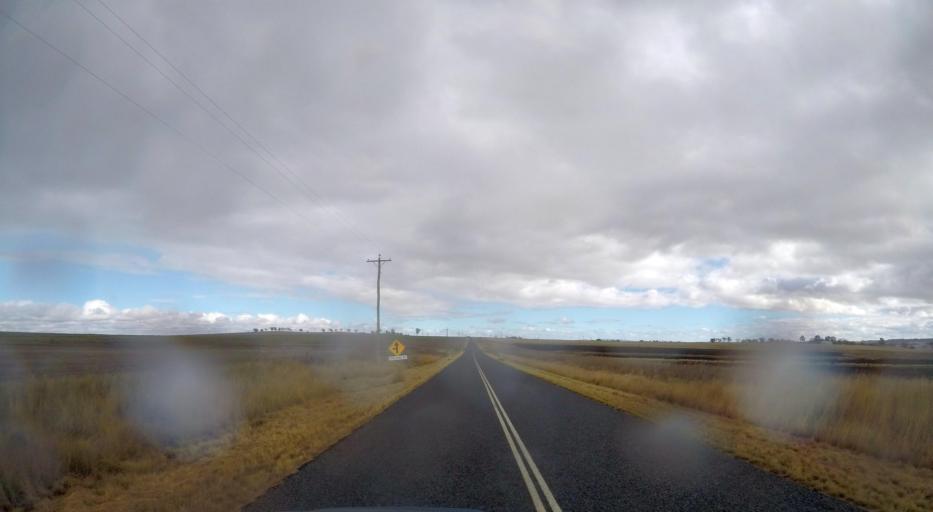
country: AU
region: Queensland
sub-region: Southern Downs
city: Warwick
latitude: -28.0547
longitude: 152.0246
